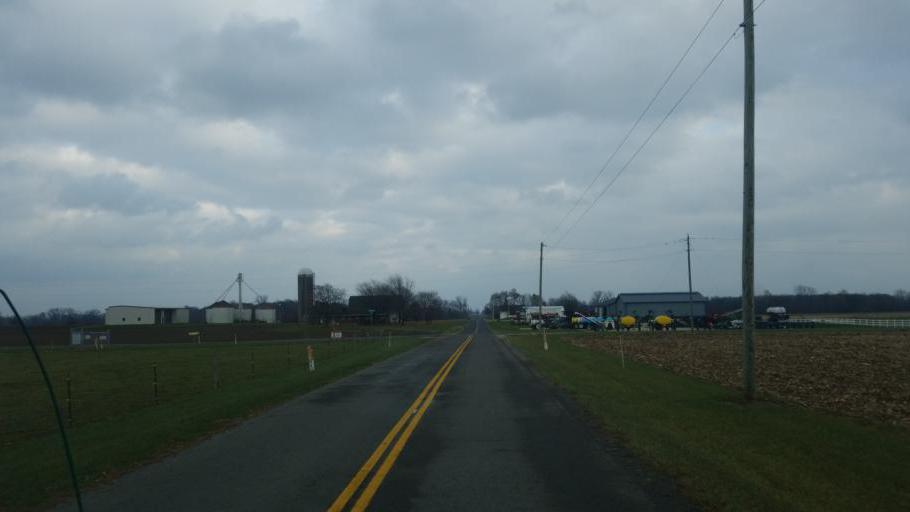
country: US
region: Ohio
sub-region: Mercer County
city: Fort Recovery
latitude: 40.5090
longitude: -84.7519
